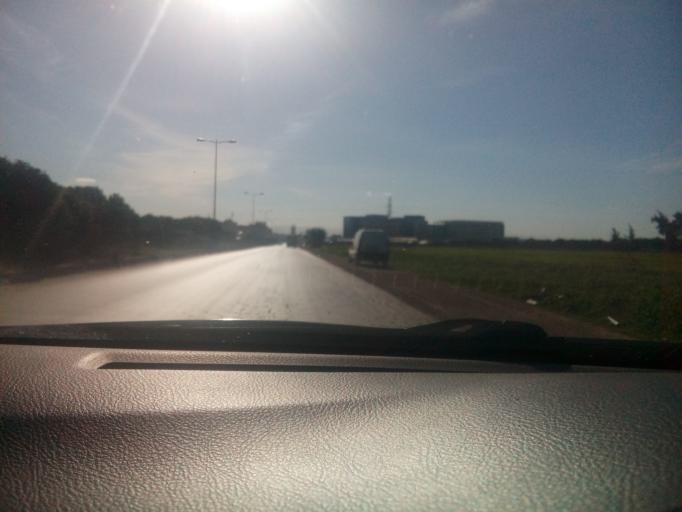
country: DZ
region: Oran
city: Sidi ech Chahmi
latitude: 35.6590
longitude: -0.5671
